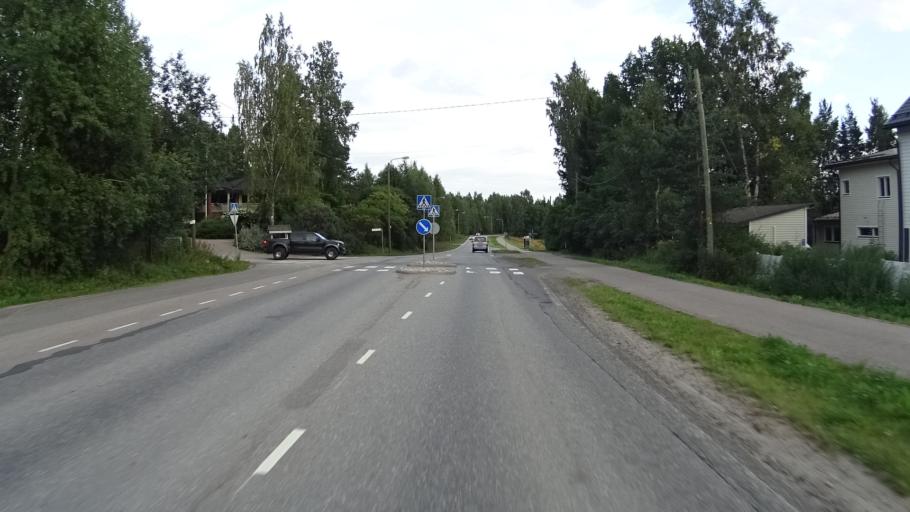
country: FI
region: Uusimaa
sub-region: Helsinki
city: Kilo
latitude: 60.3260
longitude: 24.8669
